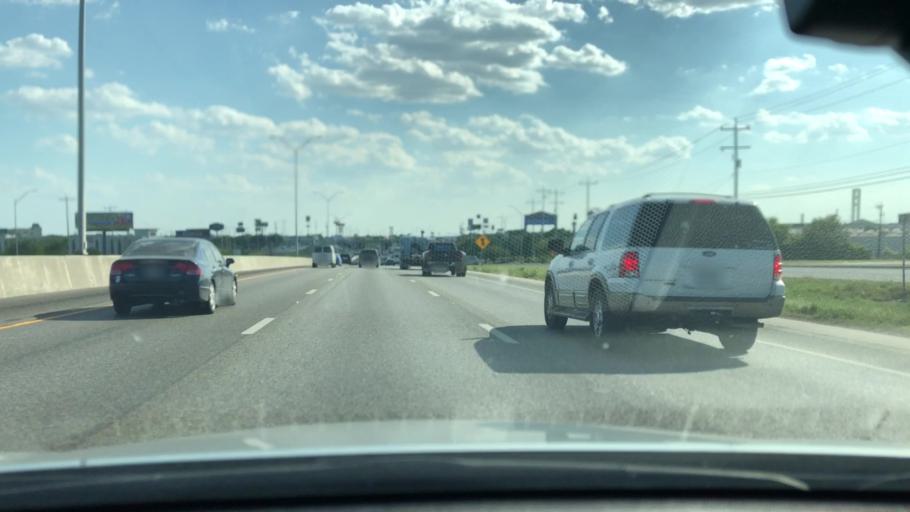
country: US
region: Texas
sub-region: Bexar County
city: Selma
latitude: 29.6040
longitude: -98.2713
